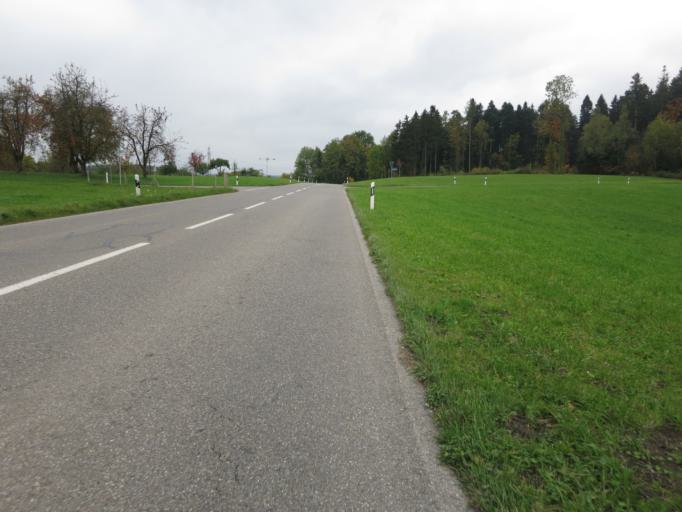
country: CH
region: Zurich
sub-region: Bezirk Hinwil
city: Wolfhausen
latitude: 47.2826
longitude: 8.7903
